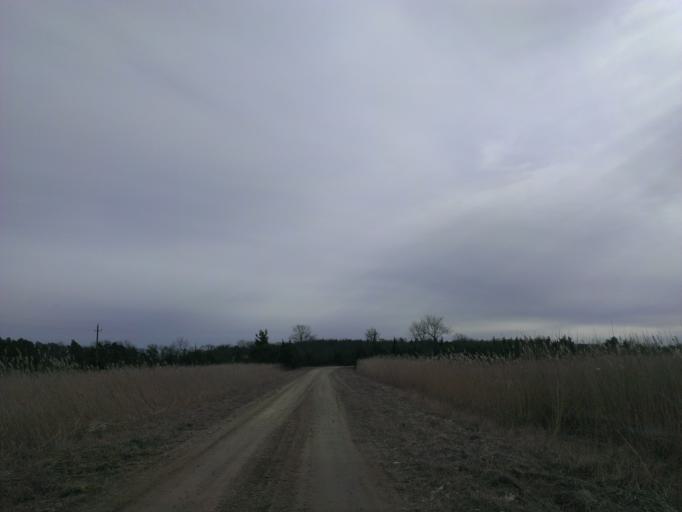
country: EE
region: Laeaene
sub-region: Lihula vald
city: Lihula
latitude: 58.5654
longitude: 23.5473
